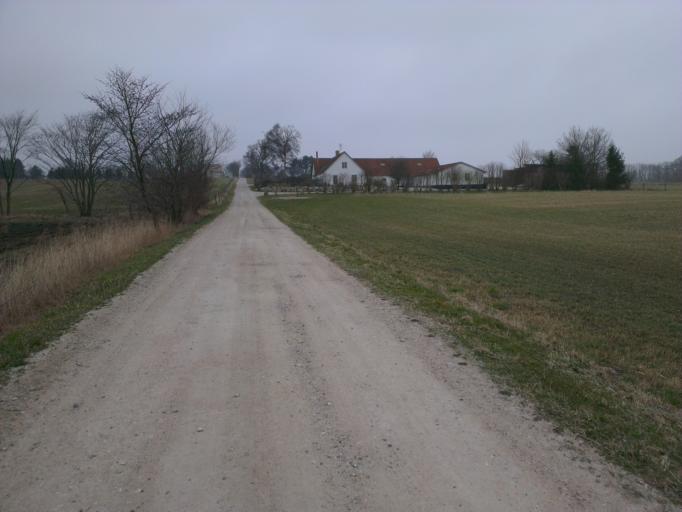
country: DK
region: Capital Region
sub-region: Frederikssund Kommune
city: Frederikssund
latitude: 55.7756
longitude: 12.0387
